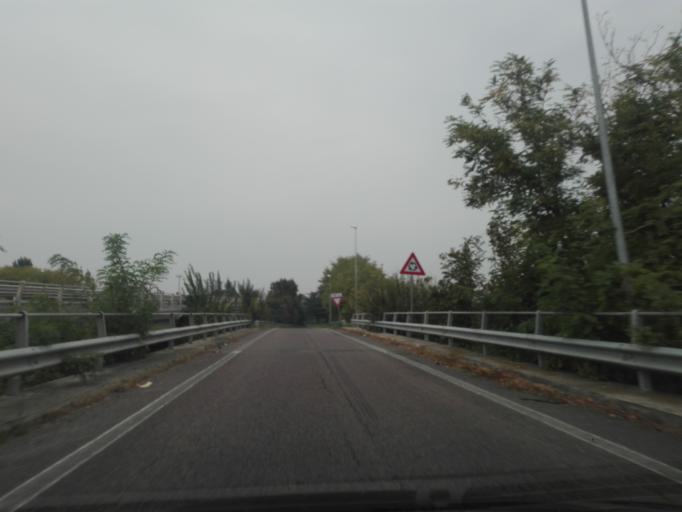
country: IT
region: Veneto
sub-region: Provincia di Verona
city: Legnago
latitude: 45.1836
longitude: 11.2701
